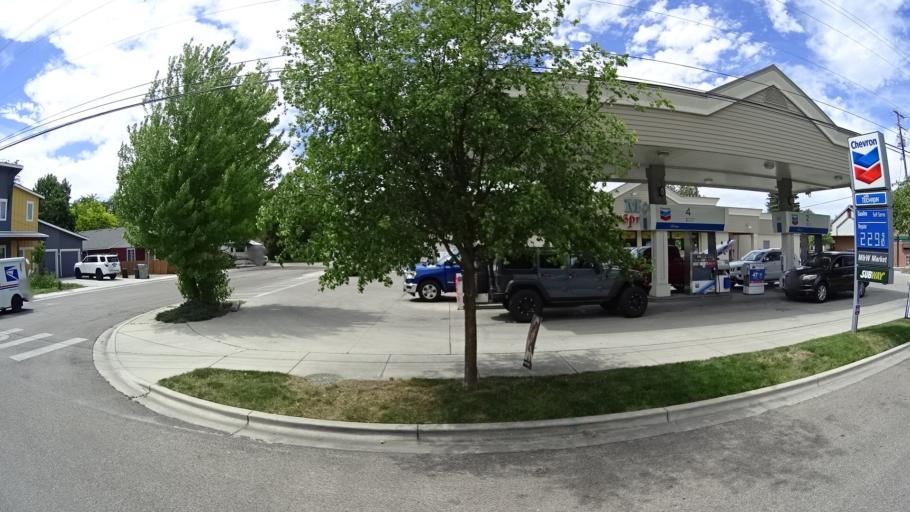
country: US
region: Idaho
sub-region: Ada County
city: Boise
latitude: 43.6027
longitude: -116.1725
